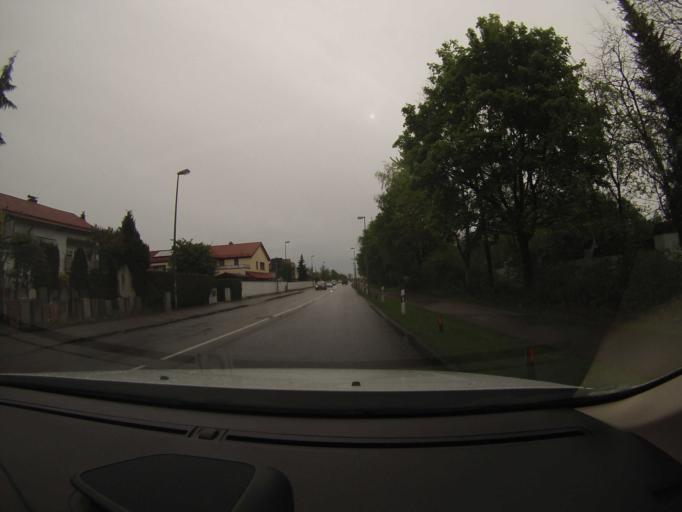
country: DE
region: Bavaria
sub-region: Upper Bavaria
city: Unterhaching
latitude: 48.0597
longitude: 11.6257
